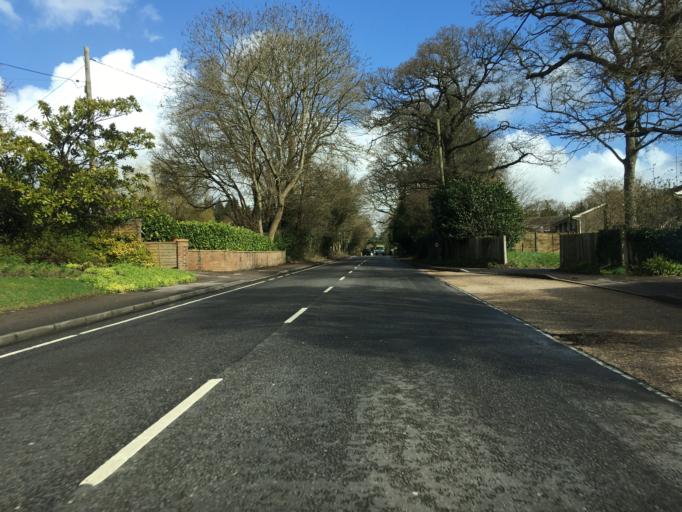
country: GB
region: England
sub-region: Hampshire
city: Compton
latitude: 51.0151
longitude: -1.3390
